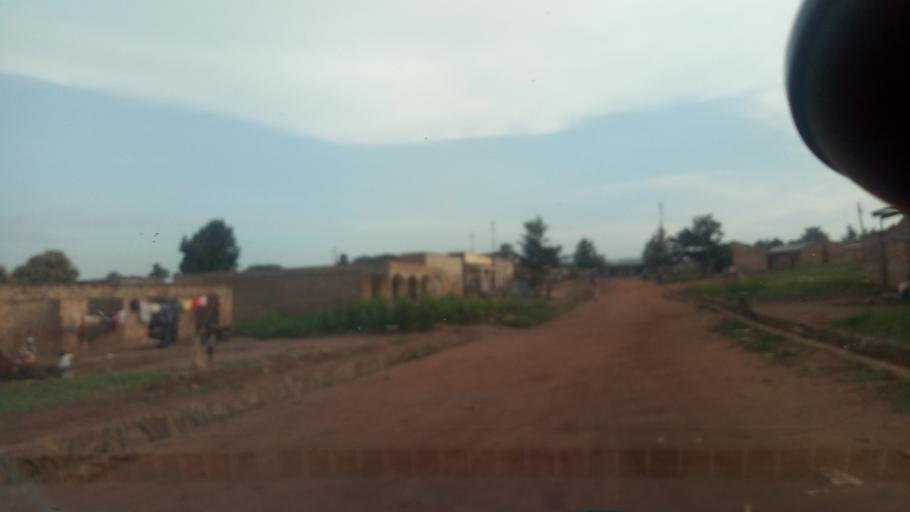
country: UG
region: Western Region
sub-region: Kiryandongo District
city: Kiryandongo
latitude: 1.8128
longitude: 32.0112
